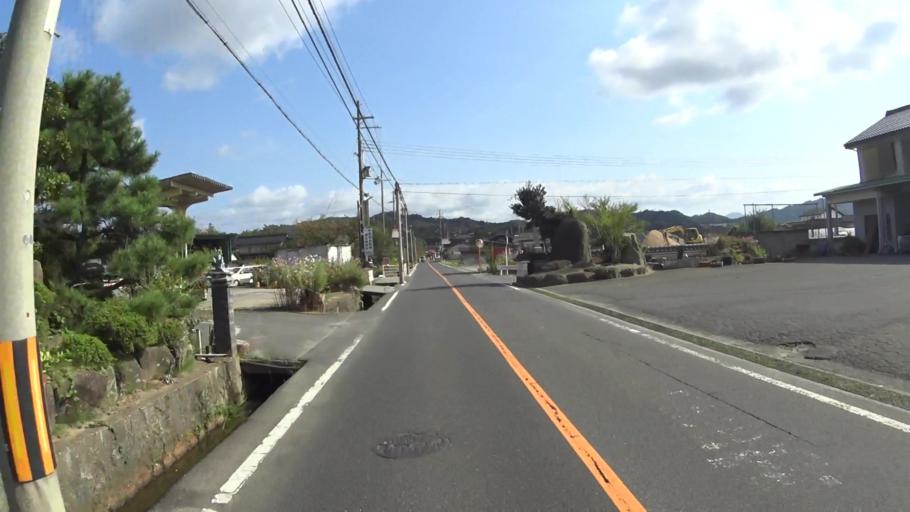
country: JP
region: Kyoto
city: Miyazu
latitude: 35.5914
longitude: 135.0996
